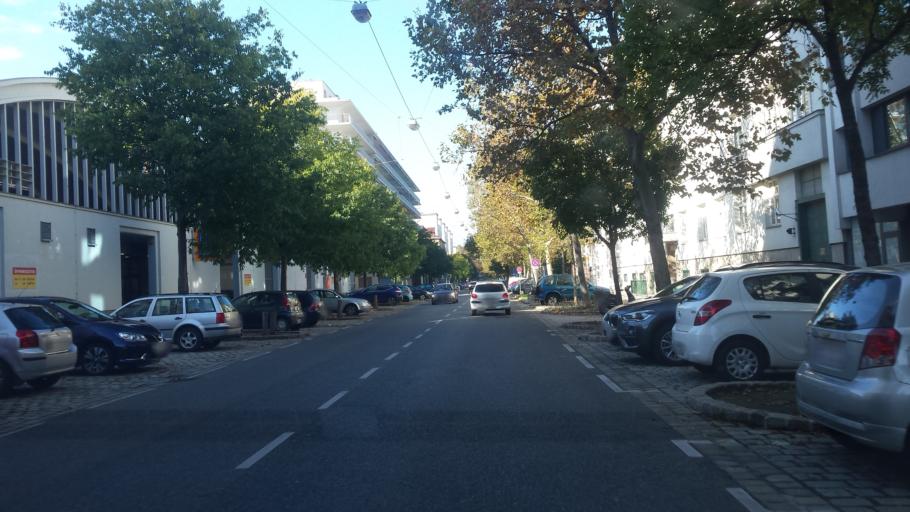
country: AT
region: Vienna
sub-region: Wien Stadt
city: Vienna
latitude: 48.2282
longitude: 16.3989
